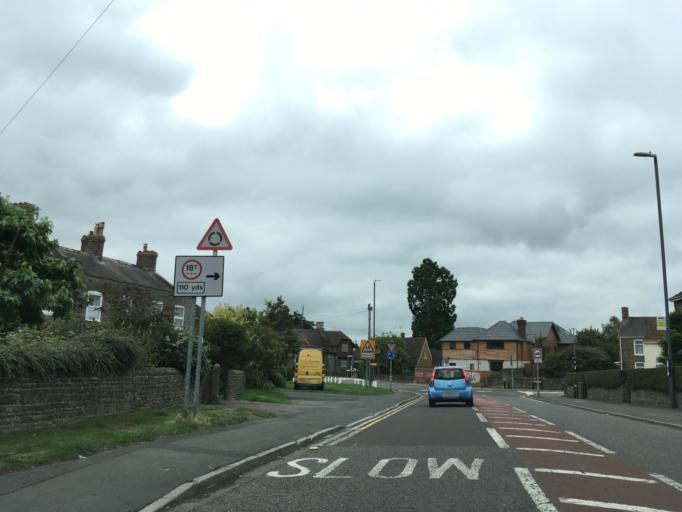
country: GB
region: England
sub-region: South Gloucestershire
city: Bitton
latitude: 51.4398
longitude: -2.4708
